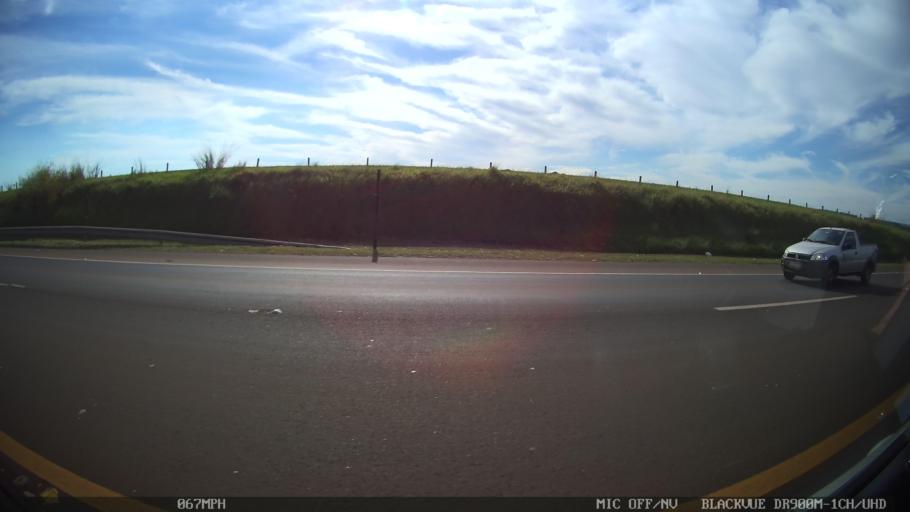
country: BR
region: Sao Paulo
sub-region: Americo Brasiliense
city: Americo Brasiliense
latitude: -21.7676
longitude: -48.0883
